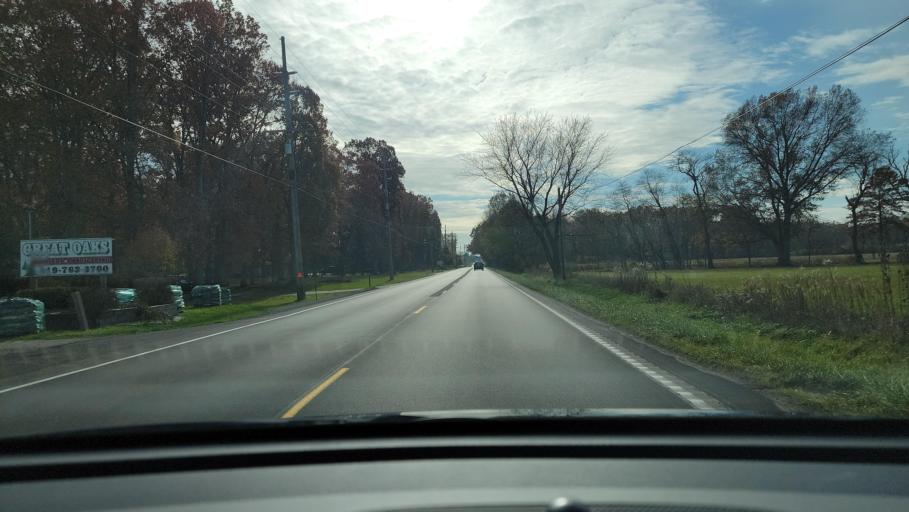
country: US
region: Indiana
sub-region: Porter County
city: South Haven
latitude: 41.5819
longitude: -87.1245
